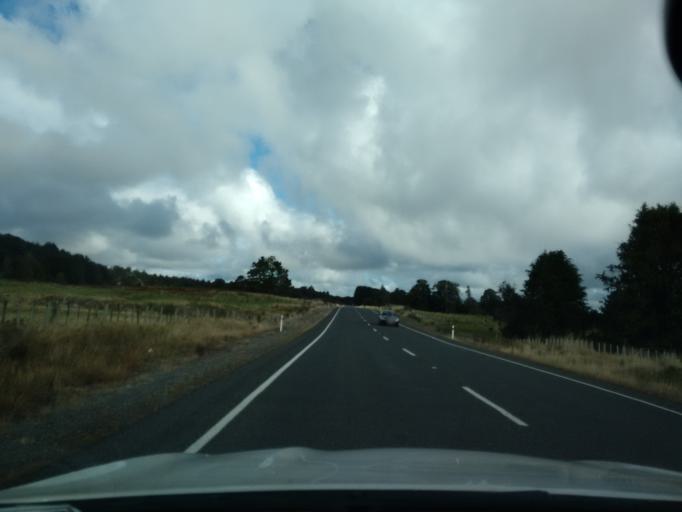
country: NZ
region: Manawatu-Wanganui
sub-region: Ruapehu District
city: Waiouru
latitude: -39.2925
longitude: 175.3876
